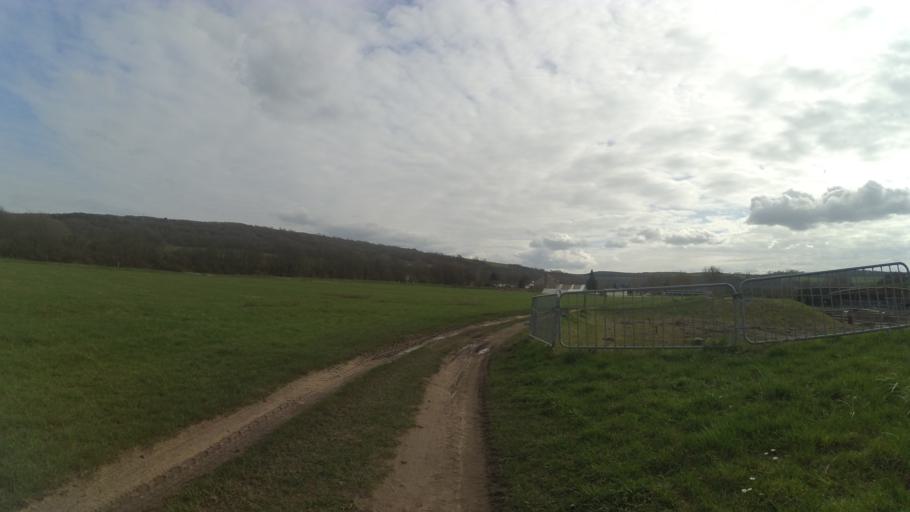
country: FR
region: Lorraine
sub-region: Departement de la Moselle
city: Bliesbruck
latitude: 49.1269
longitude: 7.1834
